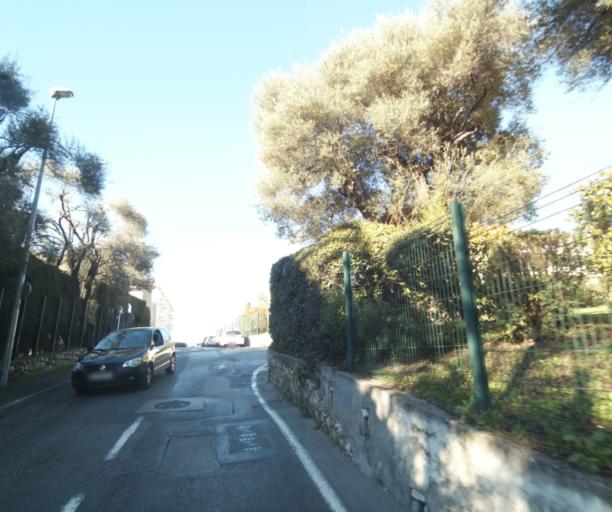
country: FR
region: Provence-Alpes-Cote d'Azur
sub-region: Departement des Alpes-Maritimes
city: Antibes
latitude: 43.5754
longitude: 7.1073
